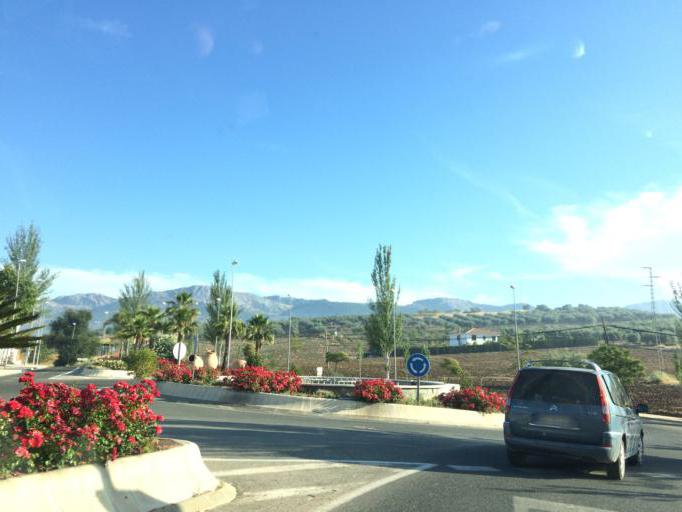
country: ES
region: Andalusia
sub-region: Provincia de Malaga
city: Colmenar
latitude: 36.9091
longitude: -4.3423
